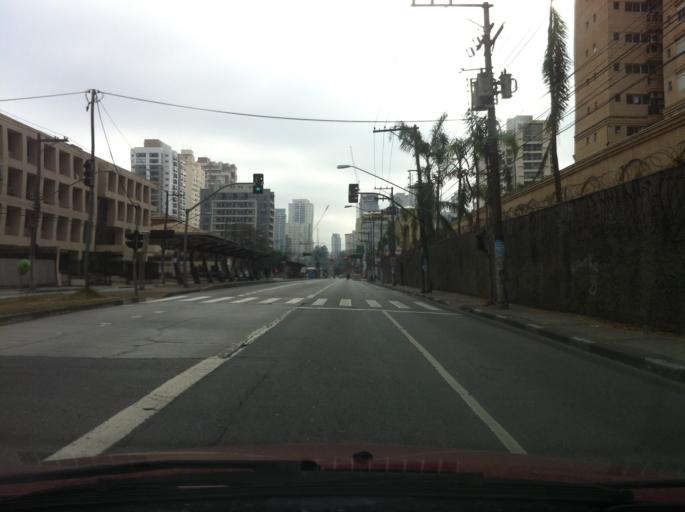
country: BR
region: Sao Paulo
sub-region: Diadema
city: Diadema
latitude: -23.6246
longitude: -46.6860
